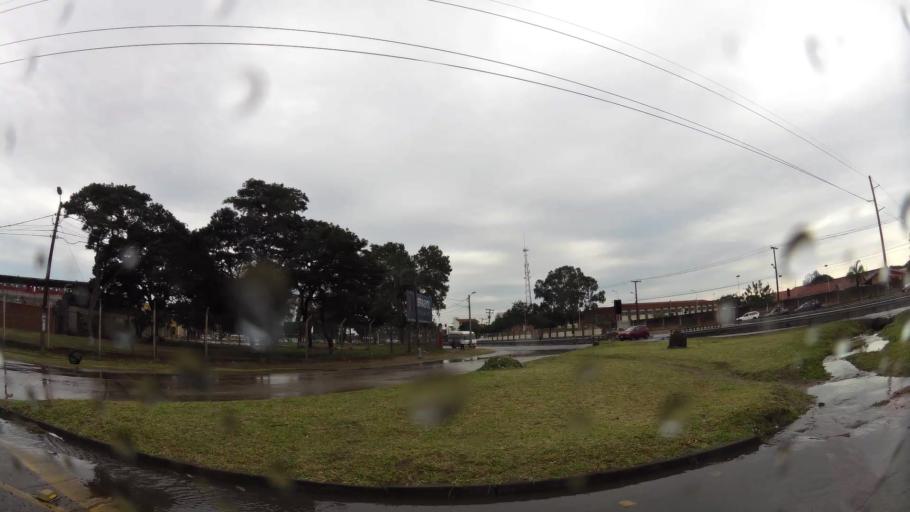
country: BO
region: Santa Cruz
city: Santa Cruz de la Sierra
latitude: -17.8060
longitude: -63.1652
